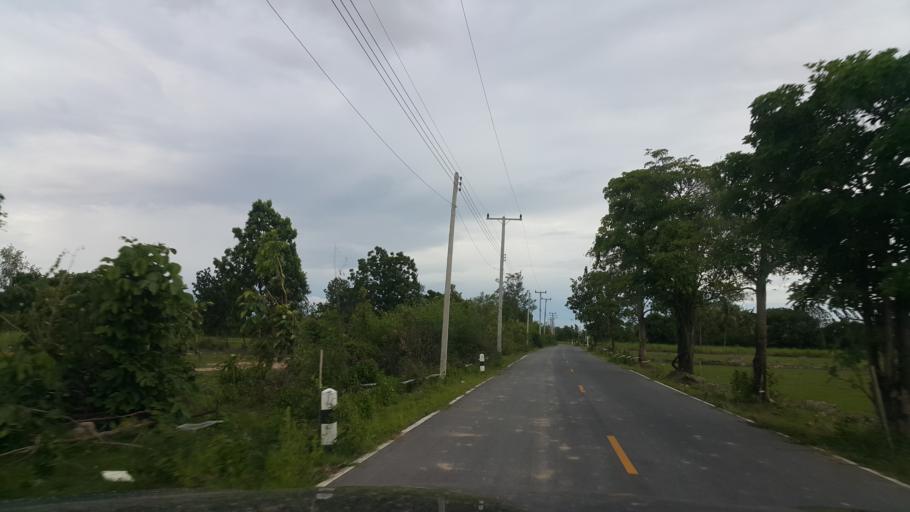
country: TH
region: Sukhothai
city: Thung Saliam
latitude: 17.1623
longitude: 99.5009
